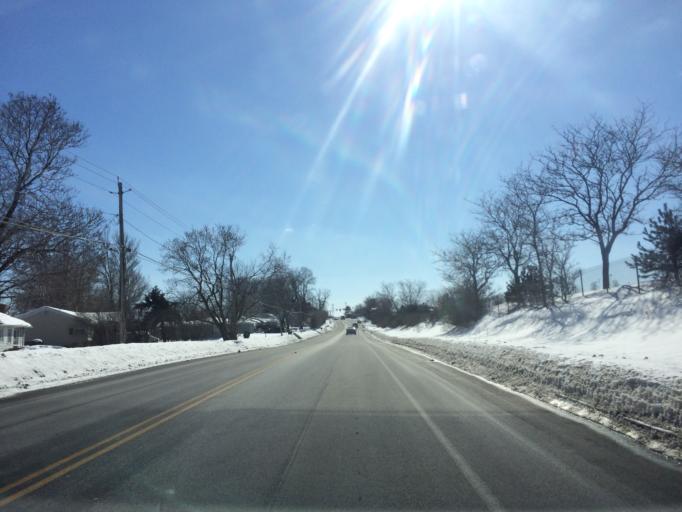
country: US
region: New York
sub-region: Monroe County
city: Rochester
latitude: 43.0983
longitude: -77.6002
